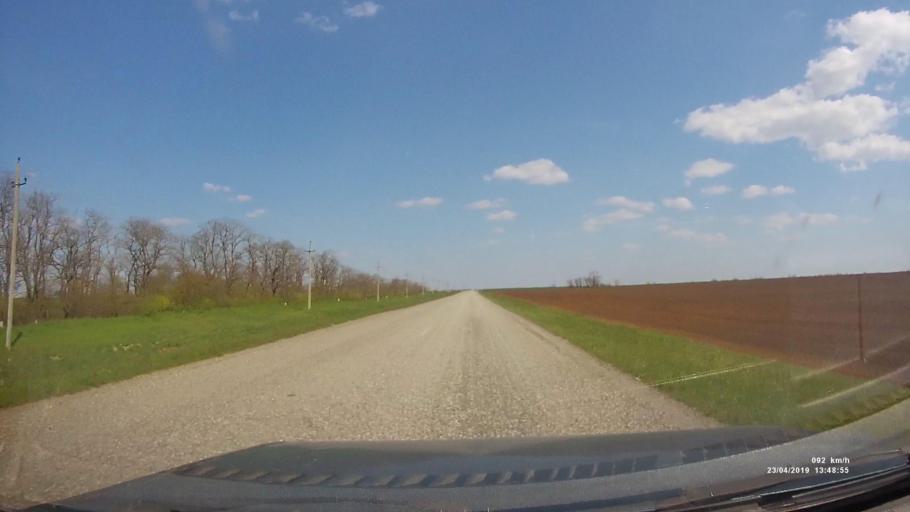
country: RU
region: Kalmykiya
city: Yashalta
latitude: 46.5993
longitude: 42.8822
